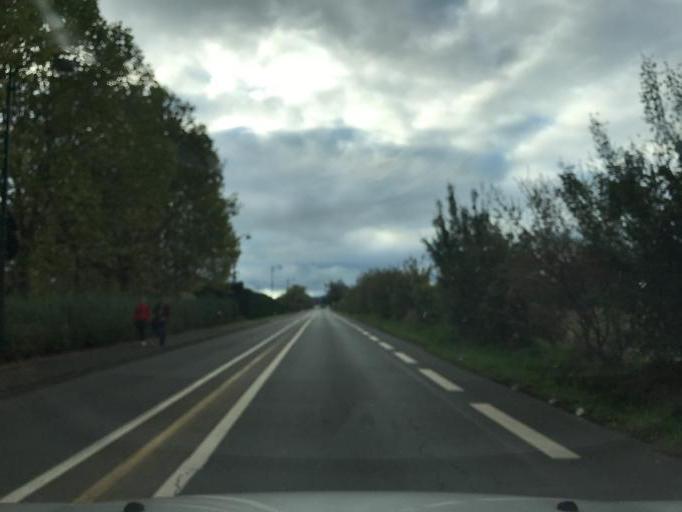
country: FR
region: Rhone-Alpes
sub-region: Departement du Rhone
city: Gleize
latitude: 45.9915
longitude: 4.6993
